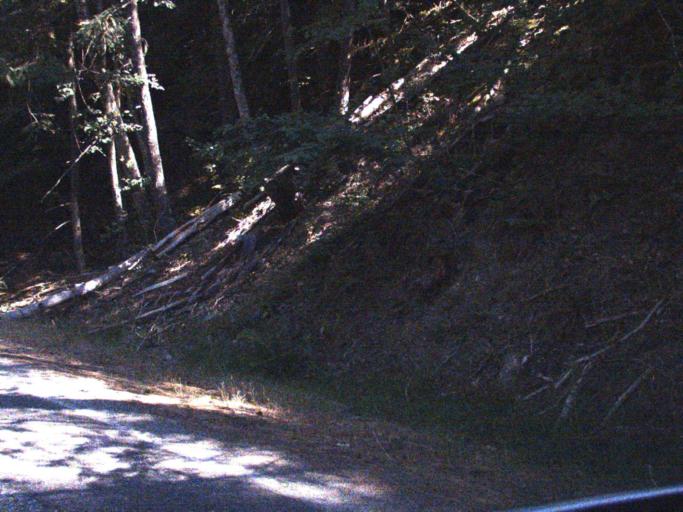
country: US
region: Washington
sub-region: King County
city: Enumclaw
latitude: 47.0197
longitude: -121.5319
